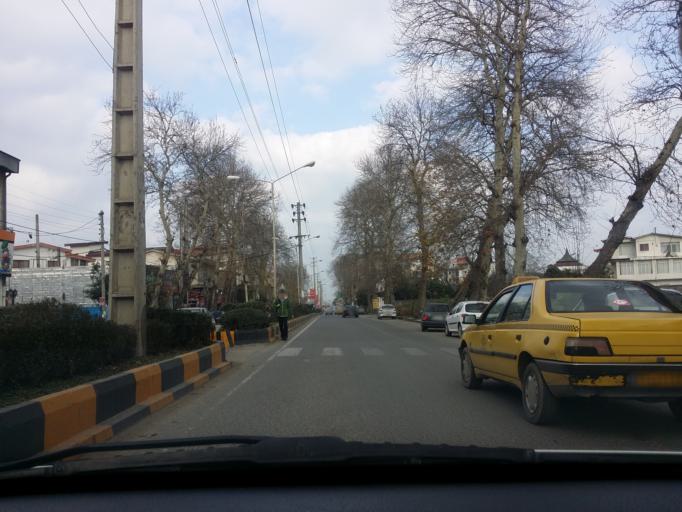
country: IR
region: Mazandaran
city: Chalus
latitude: 36.6608
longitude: 51.4132
